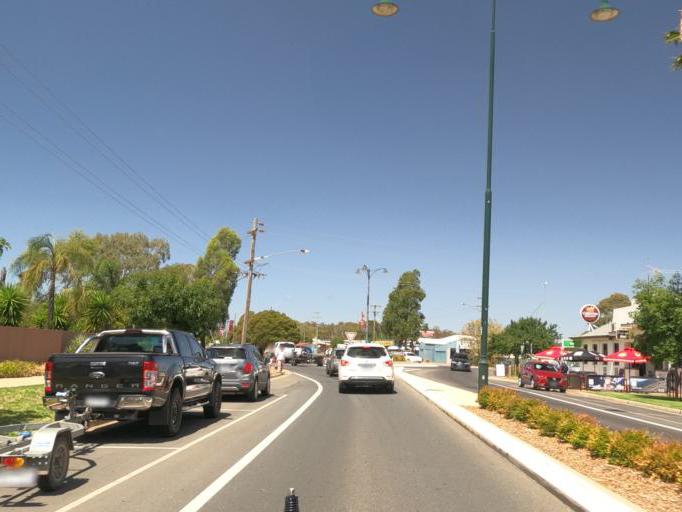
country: AU
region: New South Wales
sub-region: Corowa Shire
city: Mulwala
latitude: -35.9919
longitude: 146.0029
